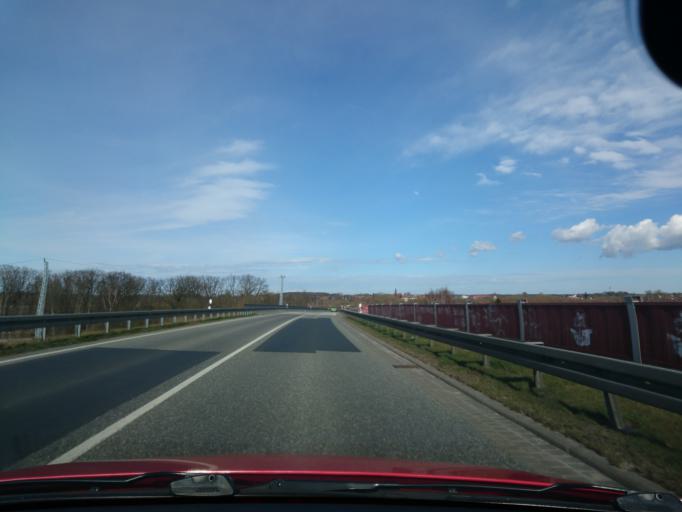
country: DE
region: Mecklenburg-Vorpommern
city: Ribnitz-Damgarten
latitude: 54.2414
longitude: 12.4580
